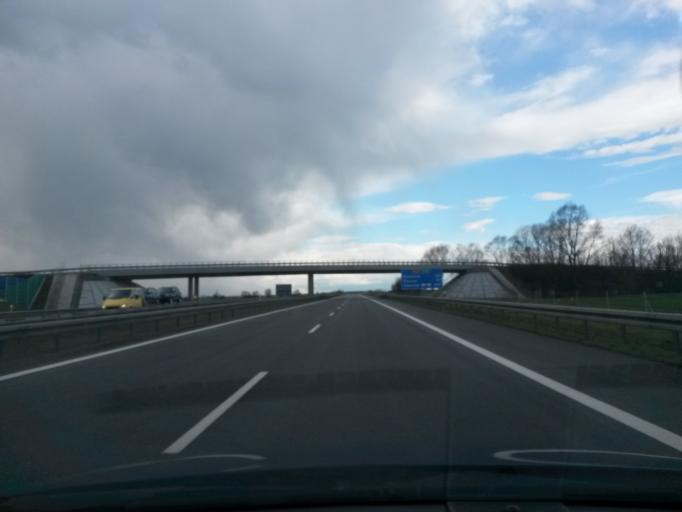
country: PL
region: Greater Poland Voivodeship
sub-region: Powiat koninski
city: Rzgow Pierwszy
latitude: 52.2075
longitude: 18.0114
